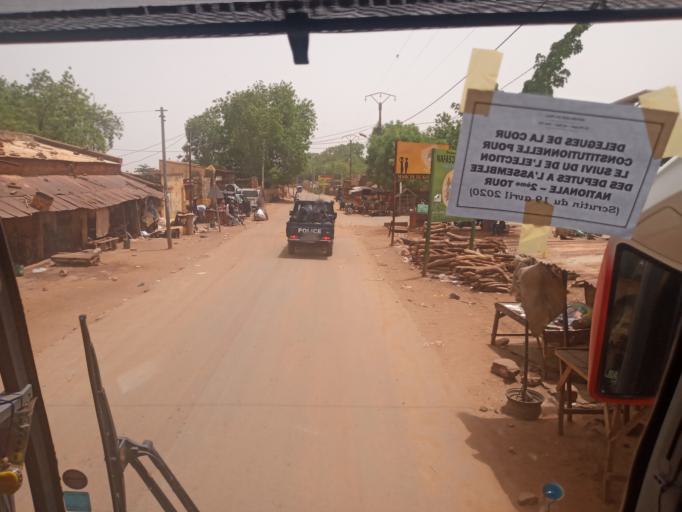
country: ML
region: Koulikoro
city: Koulikoro
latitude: 12.8883
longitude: -7.5419
